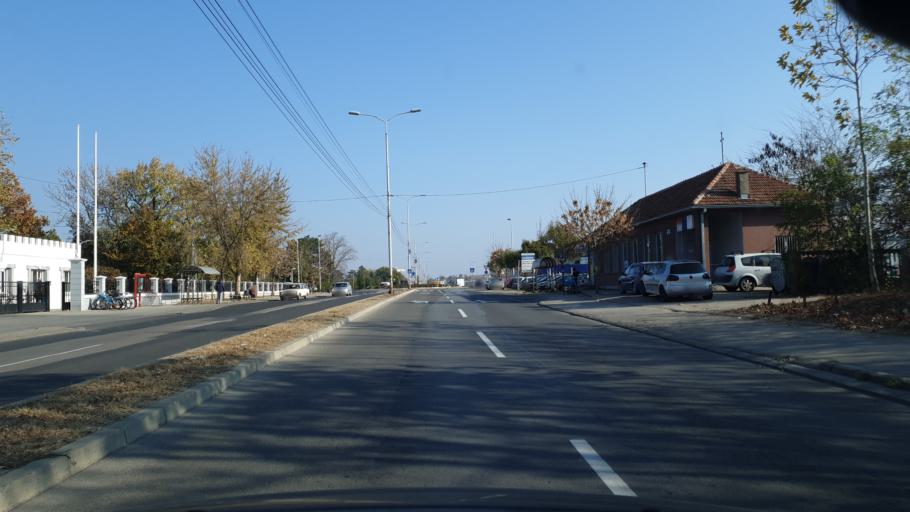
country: RS
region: Central Serbia
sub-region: Nisavski Okrug
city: Nis
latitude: 43.3180
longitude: 21.8332
